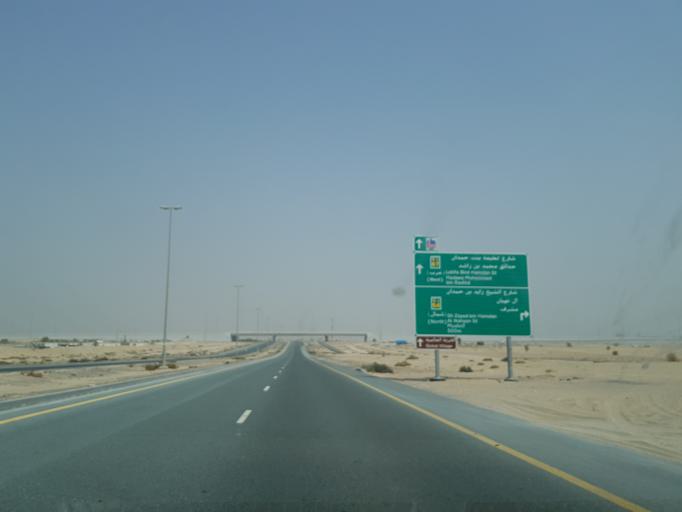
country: AE
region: Dubai
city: Dubai
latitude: 25.0538
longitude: 55.3051
